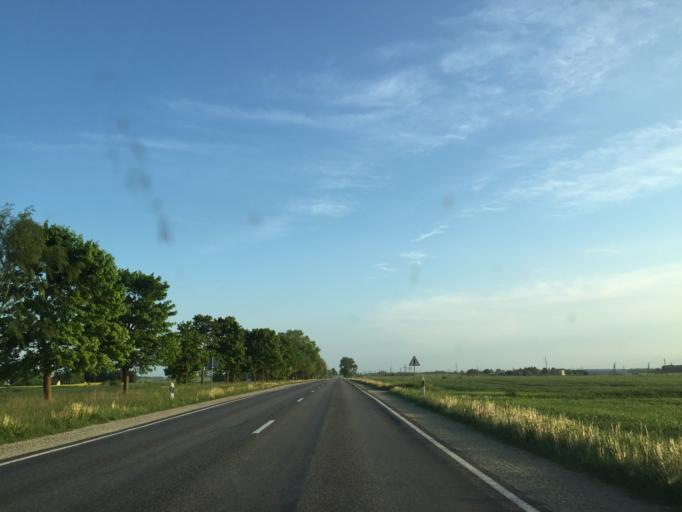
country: LT
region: Siauliu apskritis
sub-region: Siauliai
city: Siauliai
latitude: 56.0799
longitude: 23.4597
